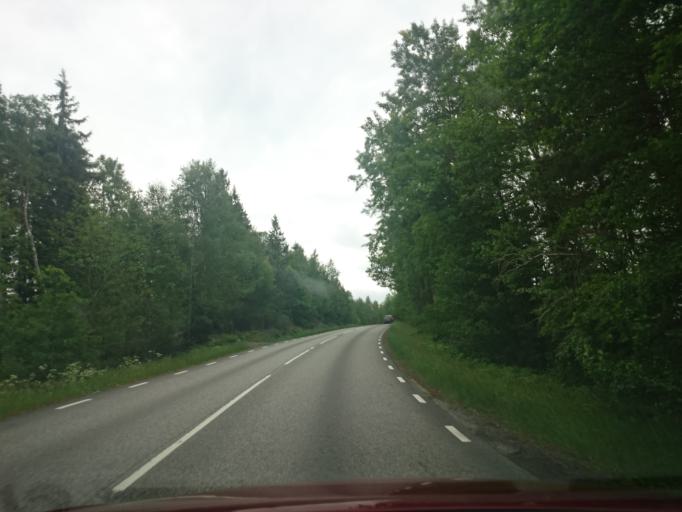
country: SE
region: Vaestra Goetaland
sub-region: Lerums Kommun
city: Stenkullen
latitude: 57.7420
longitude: 12.3389
